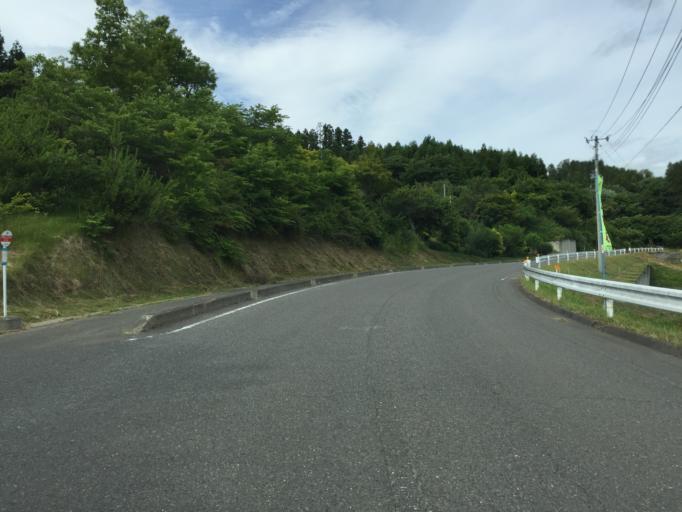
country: JP
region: Fukushima
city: Funehikimachi-funehiki
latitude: 37.5091
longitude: 140.5607
